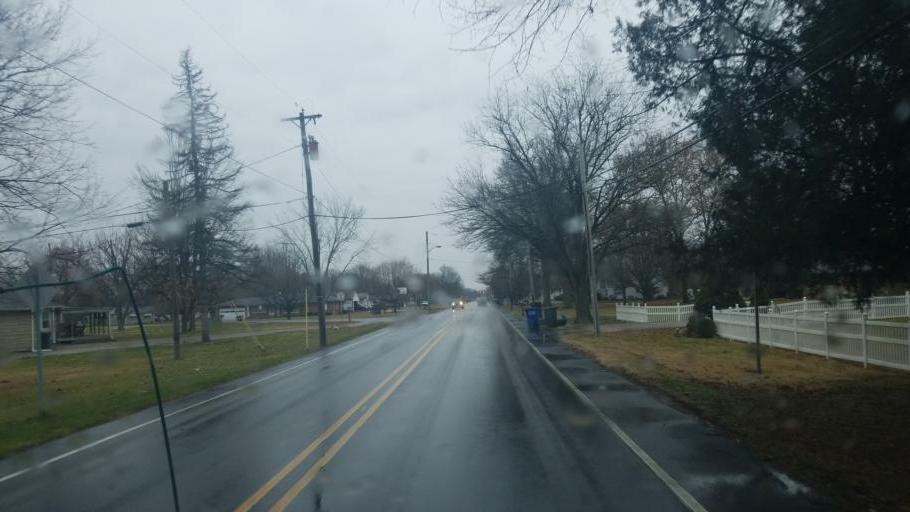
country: US
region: Indiana
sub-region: Shelby County
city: Shelbyville
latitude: 39.5086
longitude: -85.7710
